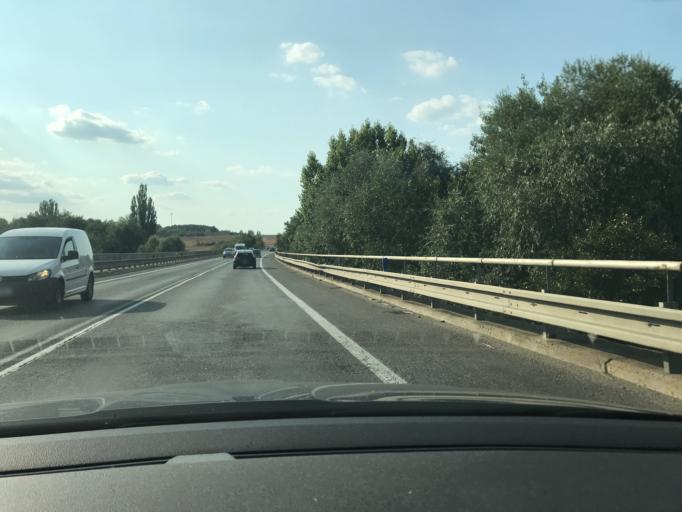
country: CZ
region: Central Bohemia
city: Klobuky
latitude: 50.2593
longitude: 14.0131
